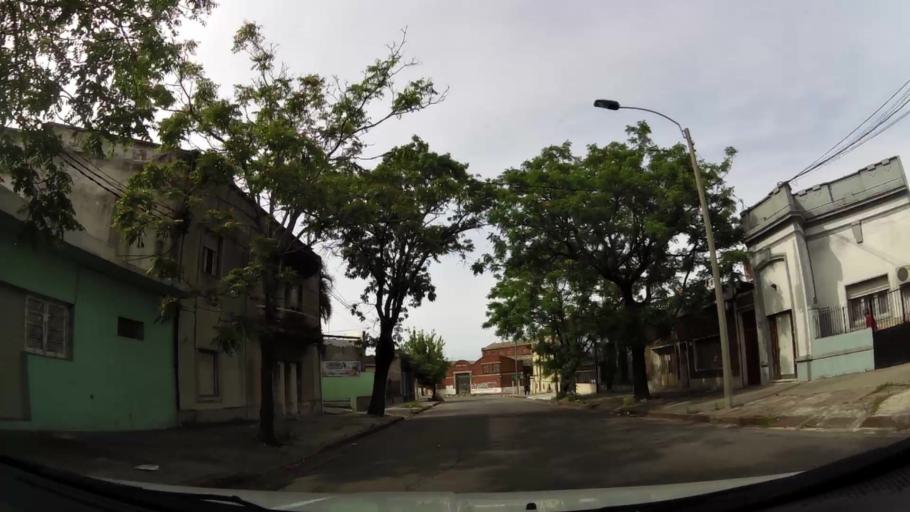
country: UY
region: Montevideo
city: Montevideo
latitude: -34.8787
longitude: -56.1995
